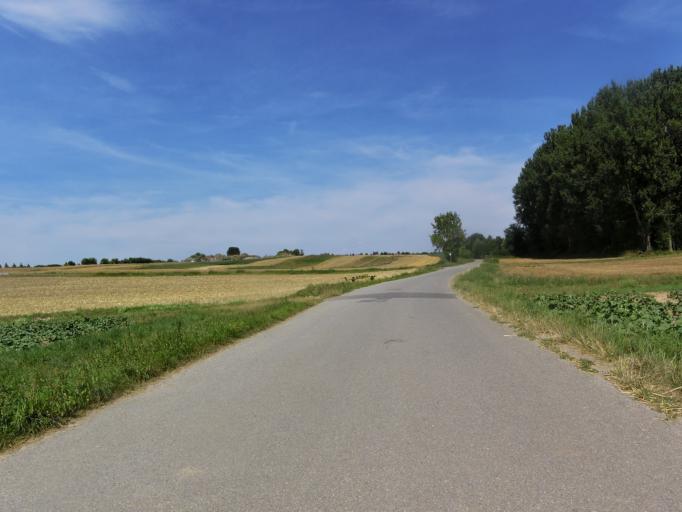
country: DE
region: Bavaria
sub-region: Regierungsbezirk Unterfranken
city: Estenfeld
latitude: 49.8158
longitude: 9.9917
